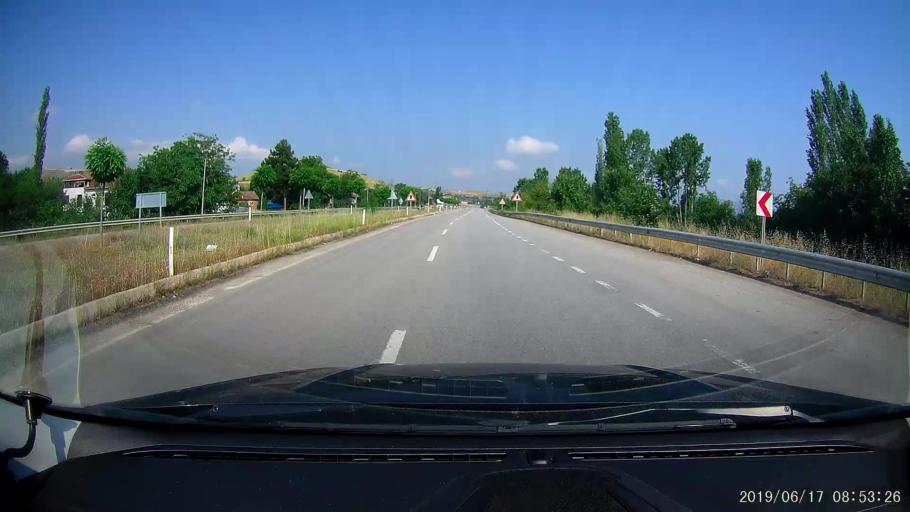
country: TR
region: Tokat
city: Erbaa
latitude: 40.7099
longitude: 36.4816
